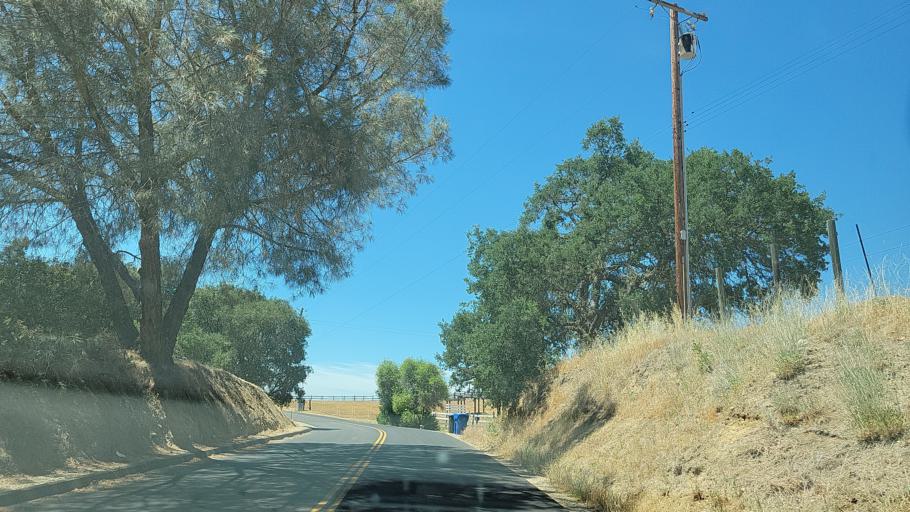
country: US
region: California
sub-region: San Luis Obispo County
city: Atascadero
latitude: 35.4785
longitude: -120.6237
